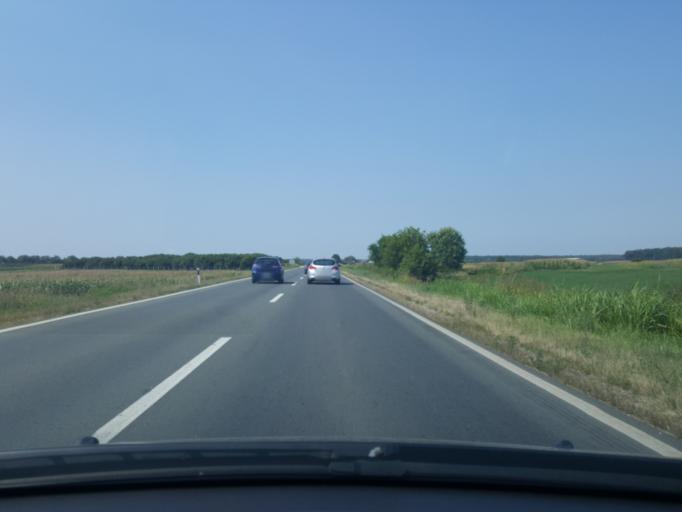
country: RS
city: Klenak
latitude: 44.7786
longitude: 19.7244
